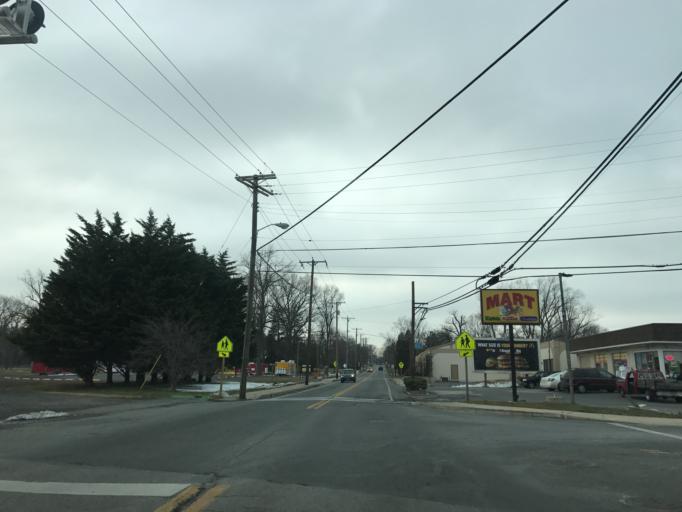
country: US
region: Maryland
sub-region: Harford County
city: Aberdeen
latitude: 39.5114
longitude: -76.1693
